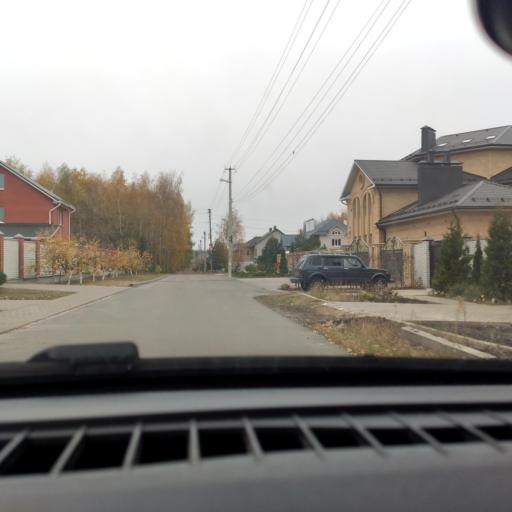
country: RU
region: Voronezj
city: Podgornoye
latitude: 51.7653
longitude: 39.1863
